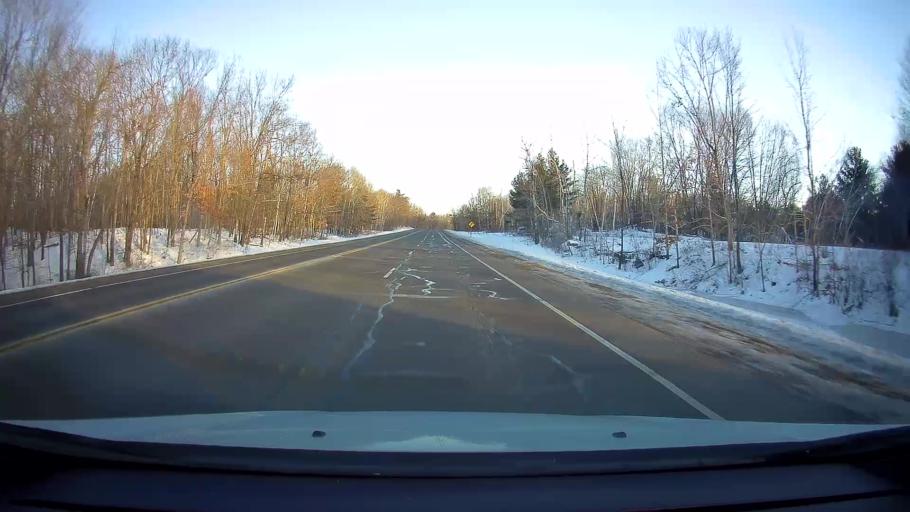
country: US
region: Wisconsin
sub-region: Barron County
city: Turtle Lake
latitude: 45.4318
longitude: -92.1295
